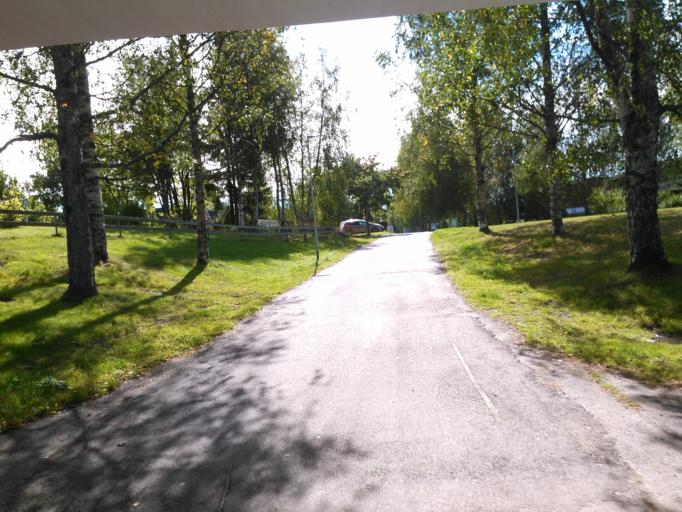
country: SE
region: Vaesterbotten
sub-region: Umea Kommun
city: Umea
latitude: 63.7985
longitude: 20.3200
